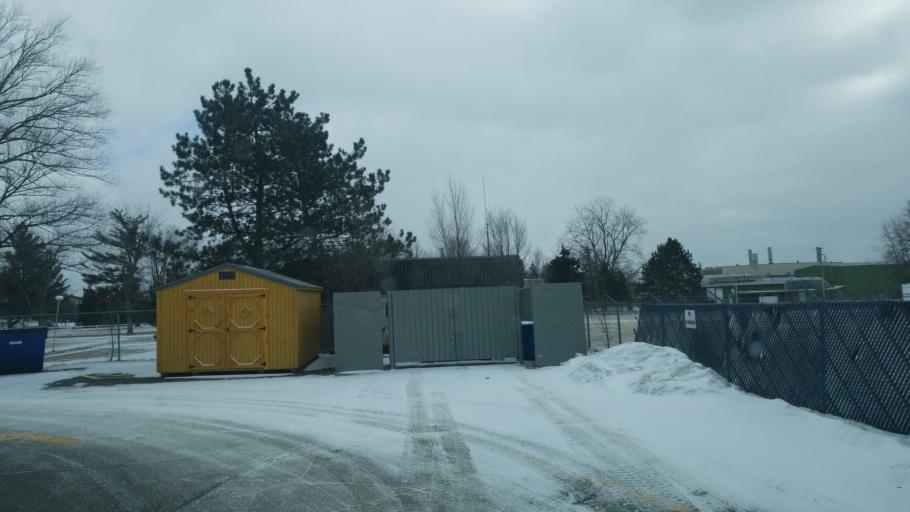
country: US
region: Michigan
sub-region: Osceola County
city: Evart
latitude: 43.8998
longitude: -85.2726
